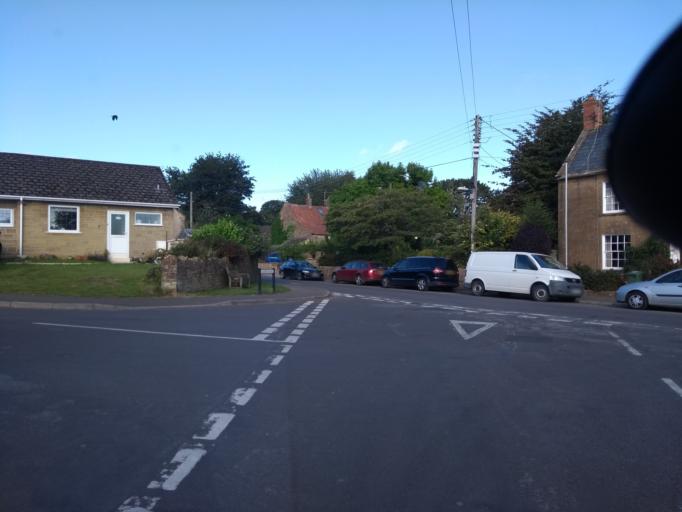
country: GB
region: England
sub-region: Somerset
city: South Petherton
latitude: 50.9490
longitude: -2.8126
